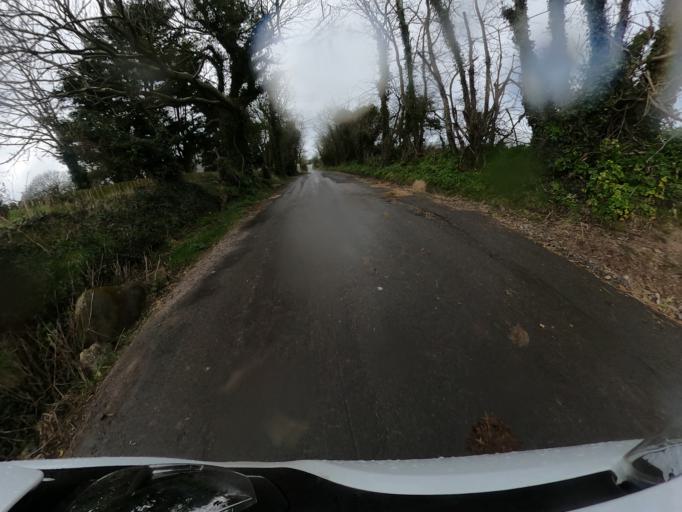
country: IM
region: Ramsey
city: Ramsey
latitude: 54.3828
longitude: -4.4658
